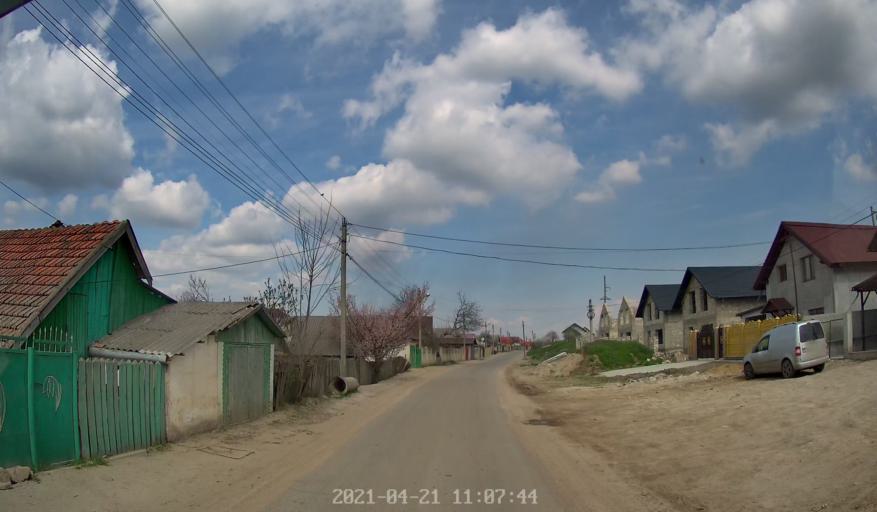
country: MD
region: Chisinau
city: Singera
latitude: 46.9504
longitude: 28.9442
